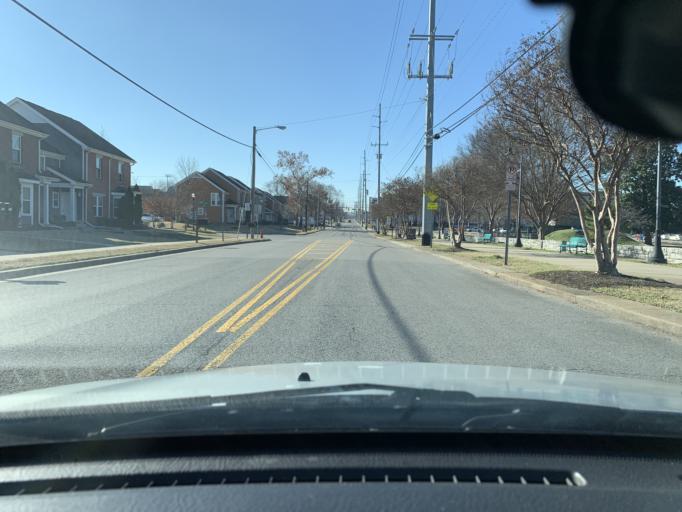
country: US
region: Tennessee
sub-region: Davidson County
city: Nashville
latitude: 36.1621
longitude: -86.7984
